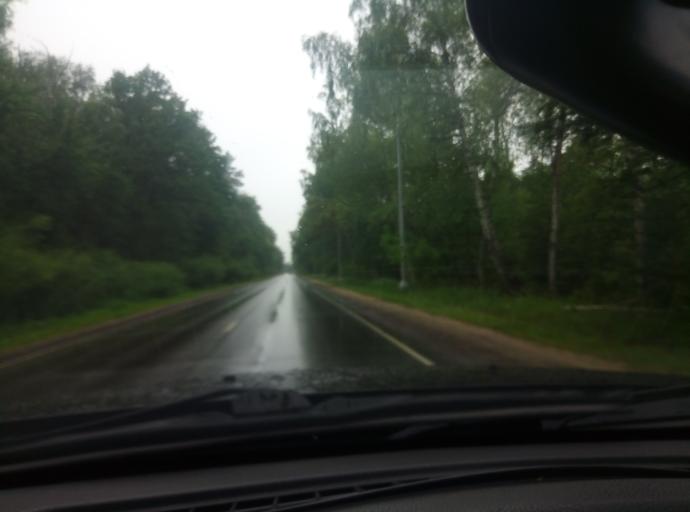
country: RU
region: Moskovskaya
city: Protvino
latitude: 54.8857
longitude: 37.1904
